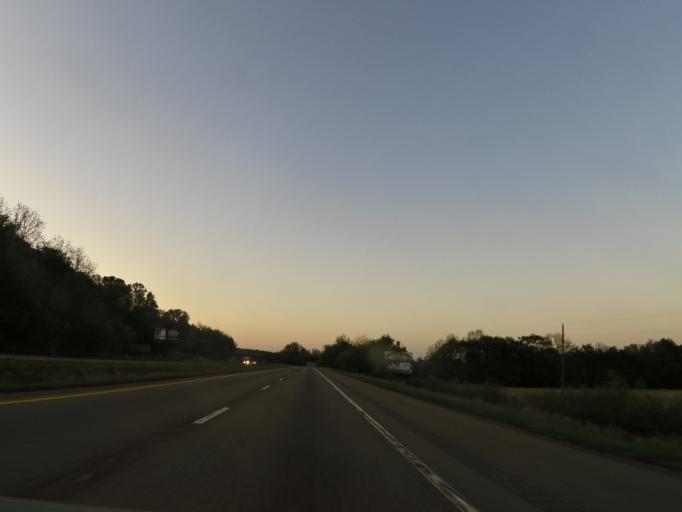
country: US
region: Tennessee
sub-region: Cocke County
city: Newport
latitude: 35.8966
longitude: -83.1845
